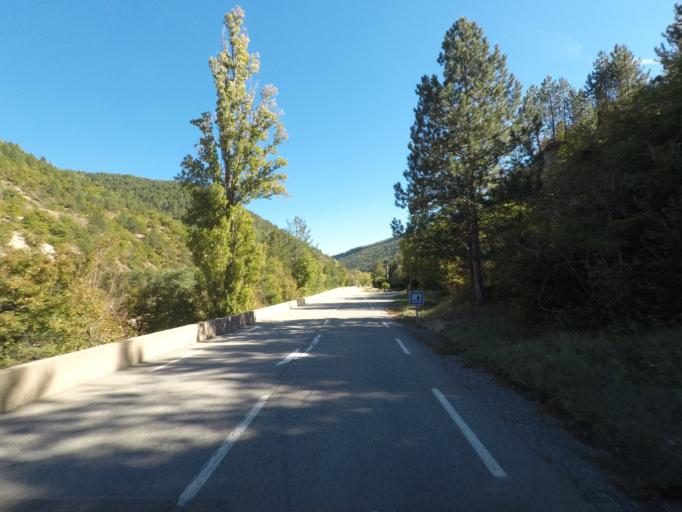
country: FR
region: Rhone-Alpes
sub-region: Departement de la Drome
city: Buis-les-Baronnies
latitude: 44.3863
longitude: 5.3924
